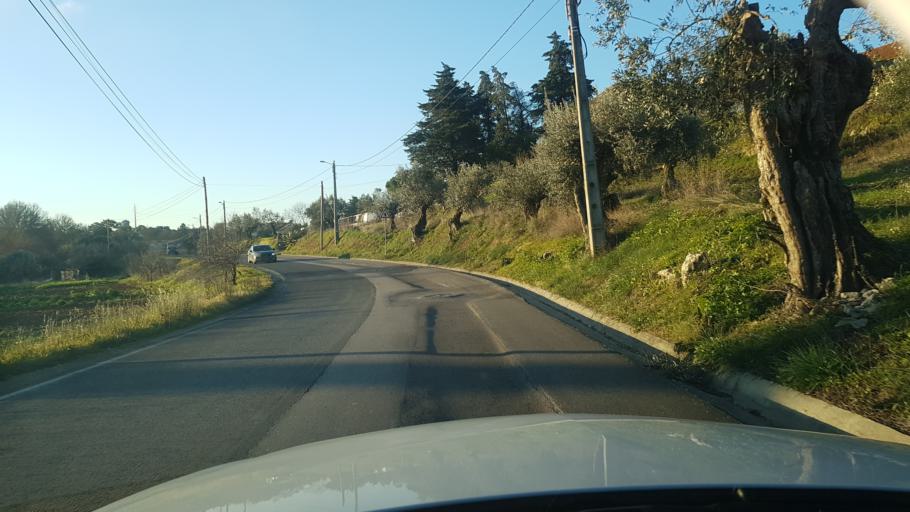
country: PT
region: Santarem
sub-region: Torres Novas
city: Torres Novas
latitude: 39.5491
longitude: -8.5522
